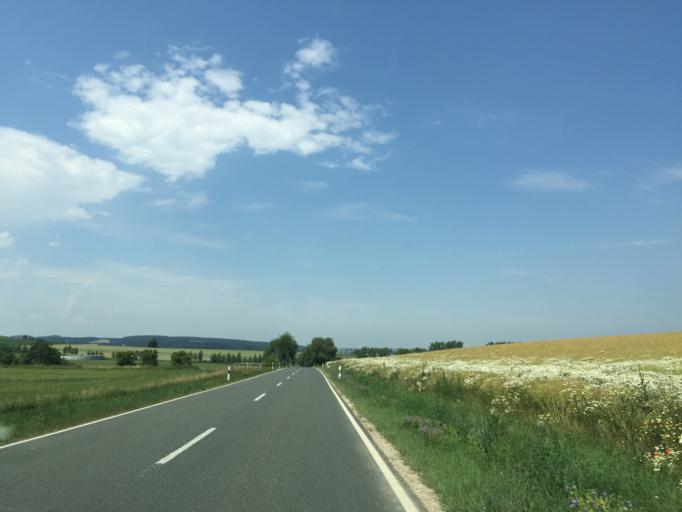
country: DE
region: Thuringia
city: Barchfeld
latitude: 50.7899
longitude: 11.1942
